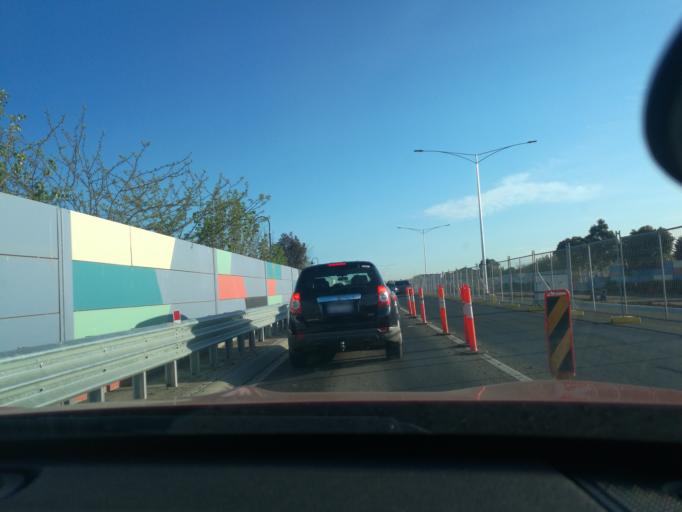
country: AU
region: Victoria
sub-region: Wyndham
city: Williams Landing
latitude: -37.8799
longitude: 144.7478
